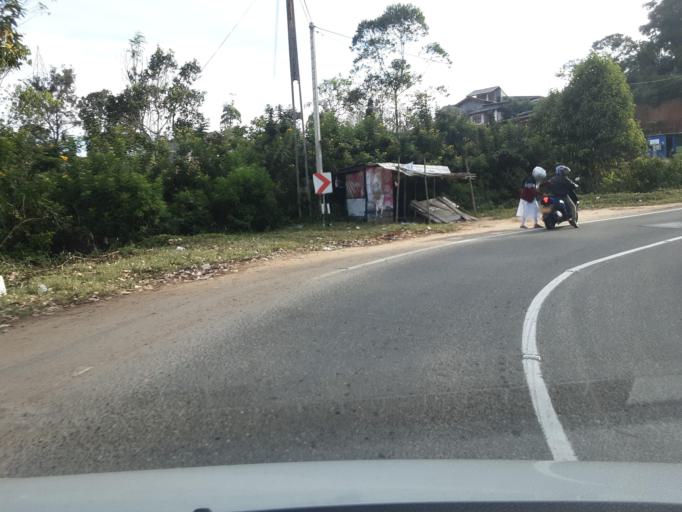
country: LK
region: Uva
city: Badulla
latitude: 6.9376
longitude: 80.9933
